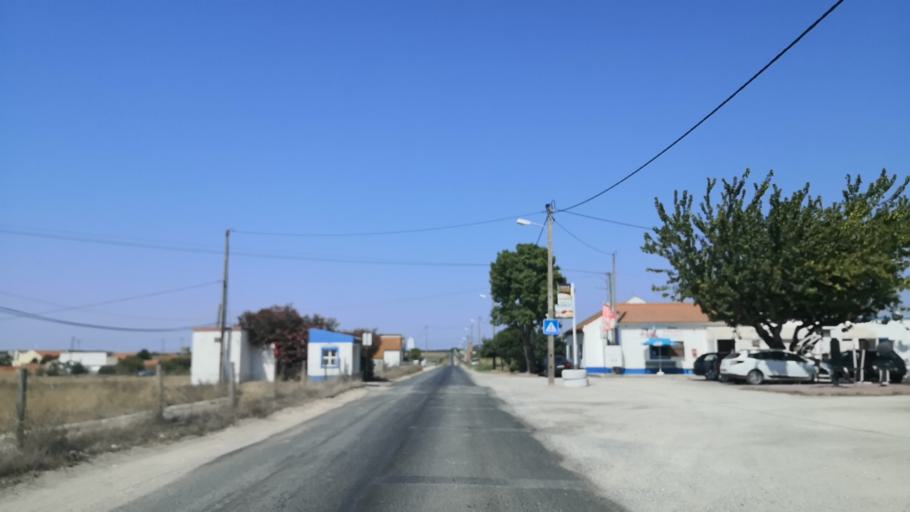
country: PT
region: Santarem
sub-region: Benavente
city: Poceirao
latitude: 38.6999
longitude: -8.7240
